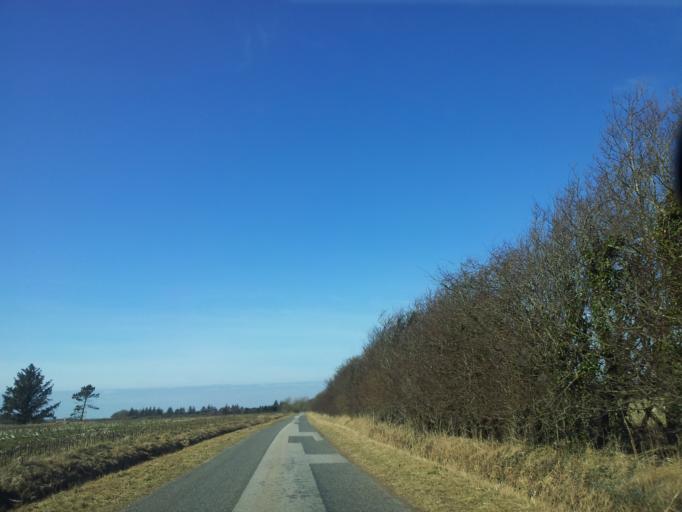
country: DK
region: South Denmark
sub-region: Tonder Kommune
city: Sherrebek
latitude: 55.2027
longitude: 8.7440
